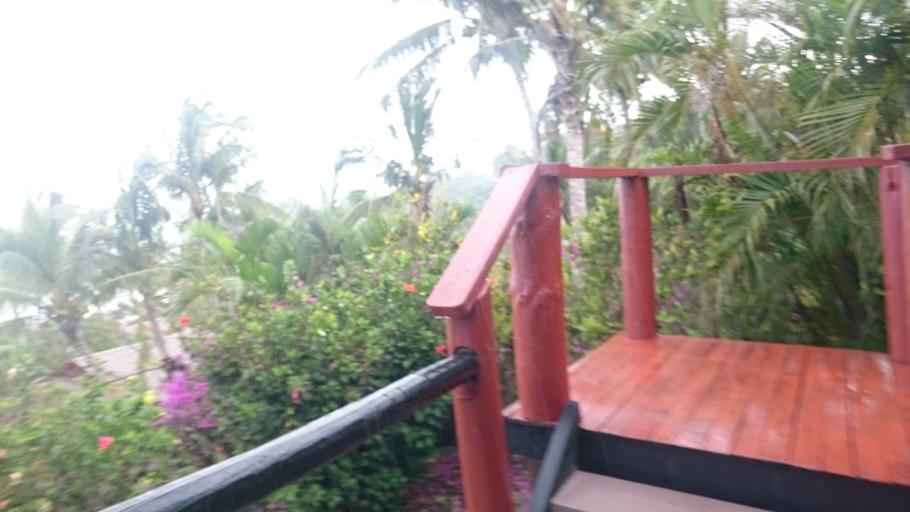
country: FJ
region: Western
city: Ba
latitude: -17.3200
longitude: 178.2054
